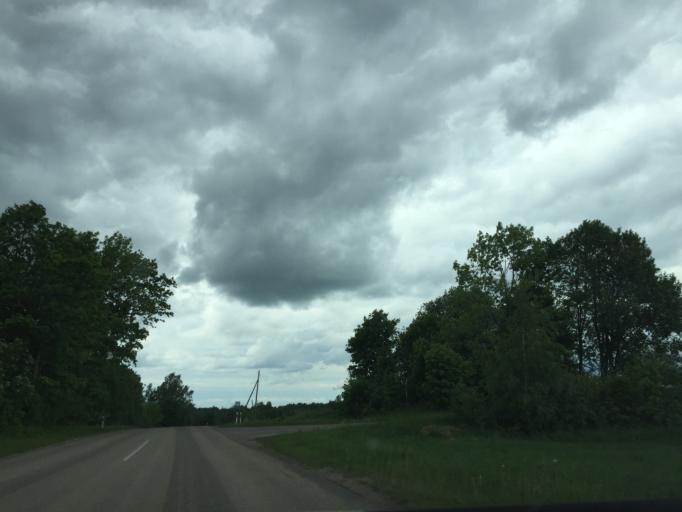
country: LV
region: Dagda
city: Dagda
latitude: 56.1243
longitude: 27.4685
